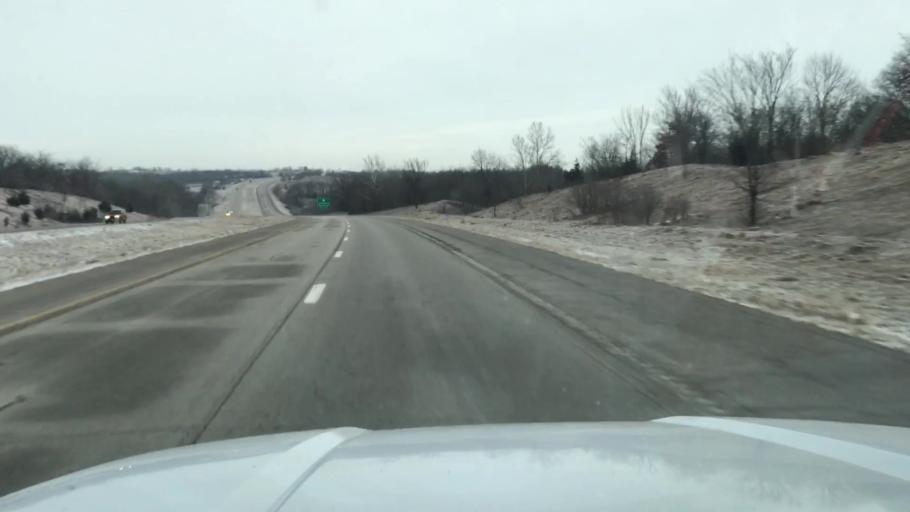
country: US
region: Missouri
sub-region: Andrew County
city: Savannah
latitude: 39.9013
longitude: -94.8572
